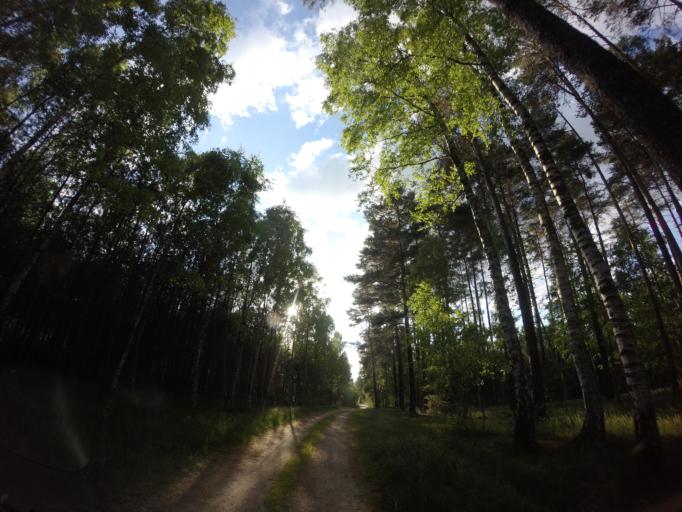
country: PL
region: West Pomeranian Voivodeship
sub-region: Powiat choszczenski
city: Drawno
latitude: 53.1938
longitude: 15.8630
